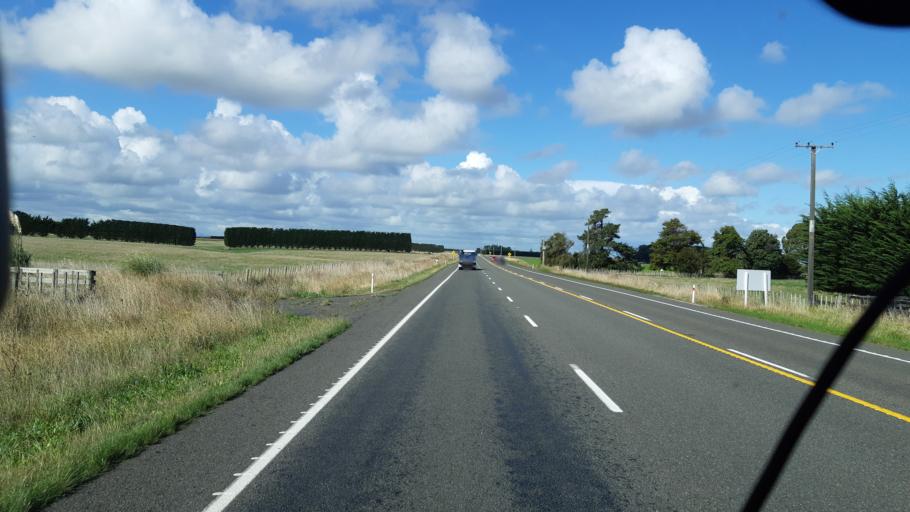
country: NZ
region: Manawatu-Wanganui
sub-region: Wanganui District
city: Wanganui
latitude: -39.9835
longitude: 175.1517
